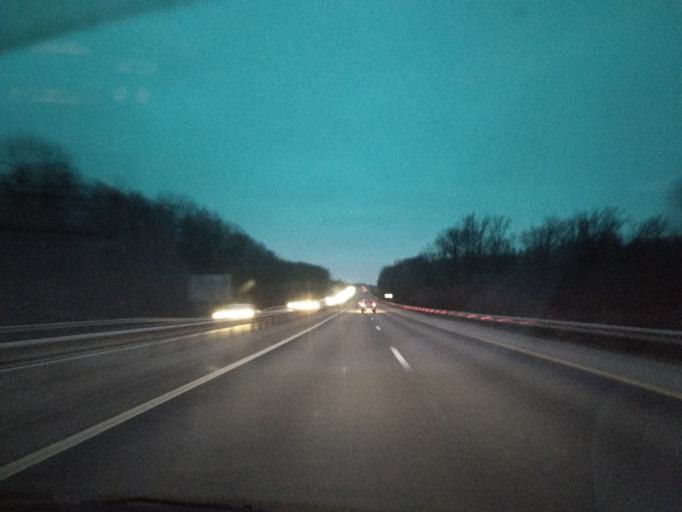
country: RU
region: Krasnodarskiy
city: Saratovskaya
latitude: 44.7570
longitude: 39.2286
